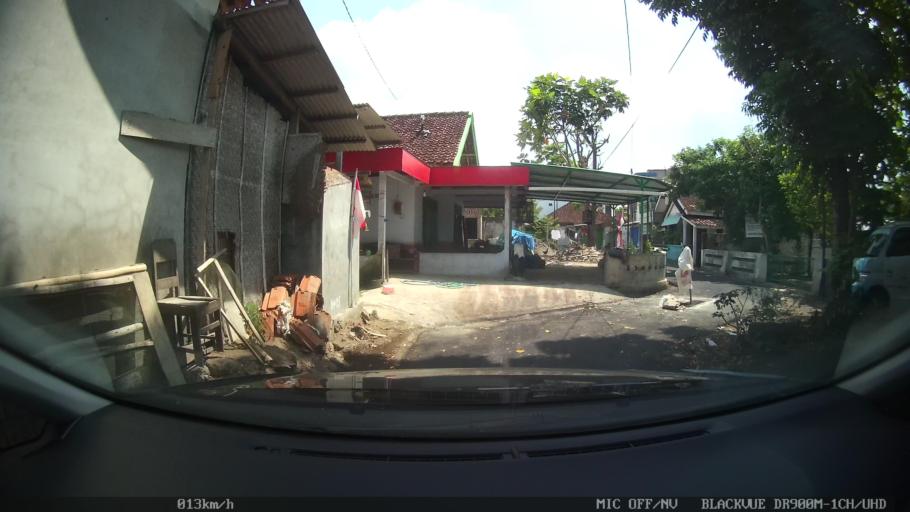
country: ID
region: Daerah Istimewa Yogyakarta
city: Sewon
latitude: -7.8424
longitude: 110.3830
